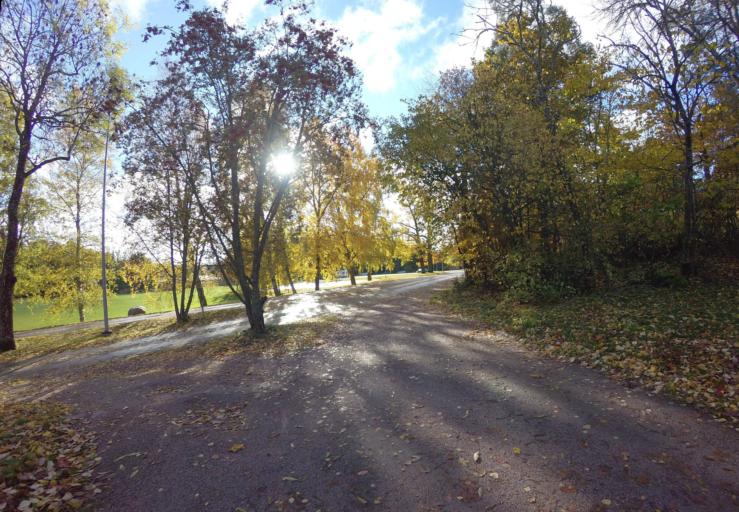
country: FI
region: Varsinais-Suomi
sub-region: Turku
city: Naantali
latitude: 60.4241
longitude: 22.0949
